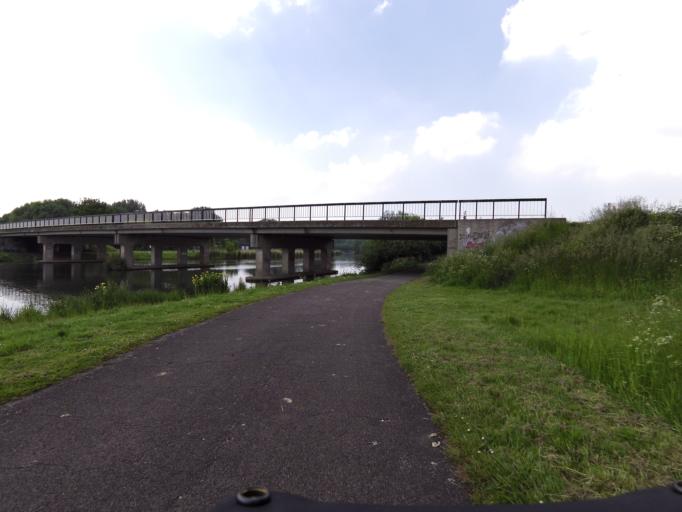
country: NL
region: South Holland
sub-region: Gemeente Spijkenisse
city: Spijkenisse
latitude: 51.8249
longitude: 4.2675
